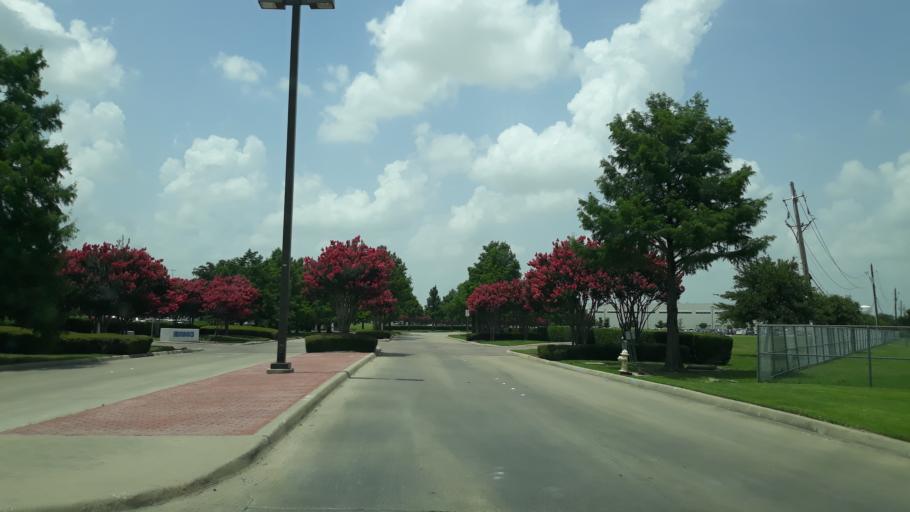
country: US
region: Texas
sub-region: Dallas County
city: Coppell
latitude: 32.9345
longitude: -97.0053
